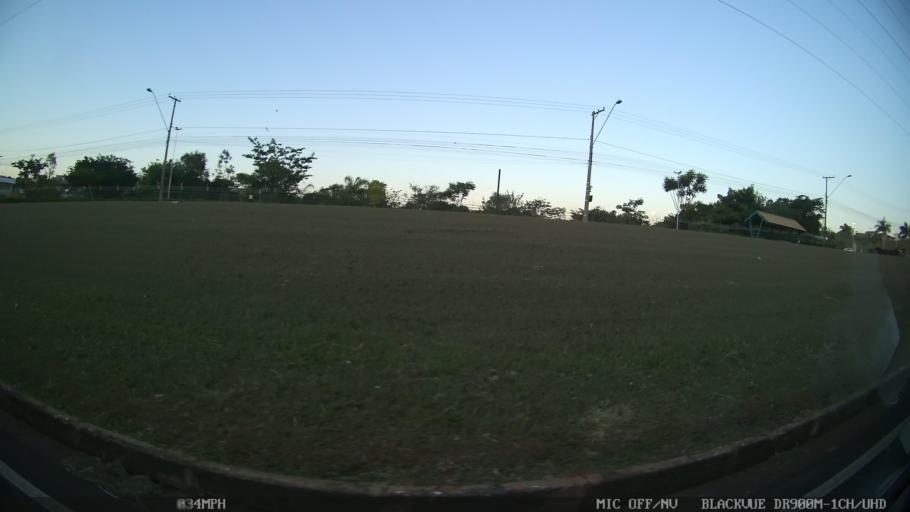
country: BR
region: Sao Paulo
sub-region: Sao Jose Do Rio Preto
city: Sao Jose do Rio Preto
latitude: -20.8125
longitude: -49.3404
